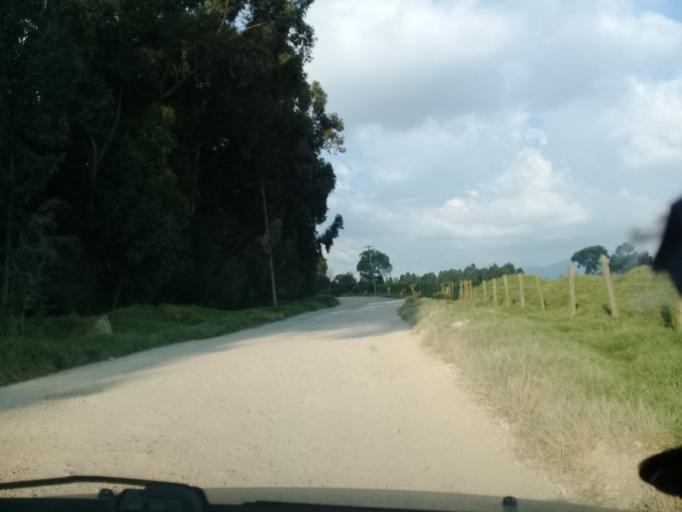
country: CO
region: Cundinamarca
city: Funza
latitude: 4.7629
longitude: -74.2215
